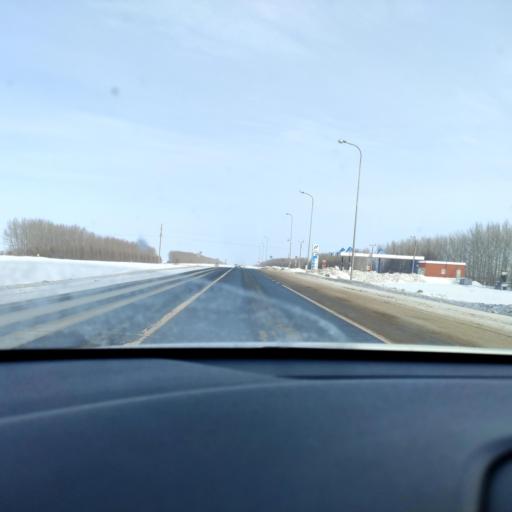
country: RU
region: Ulyanovsk
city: Tsil'na
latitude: 54.7632
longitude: 48.1940
